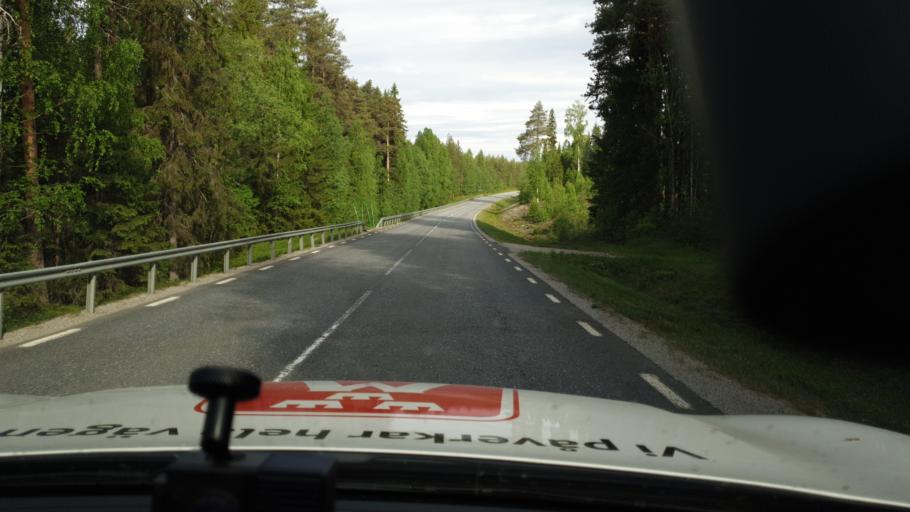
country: SE
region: Vaesterbotten
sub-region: Lycksele Kommun
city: Lycksele
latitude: 64.4559
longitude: 18.9123
